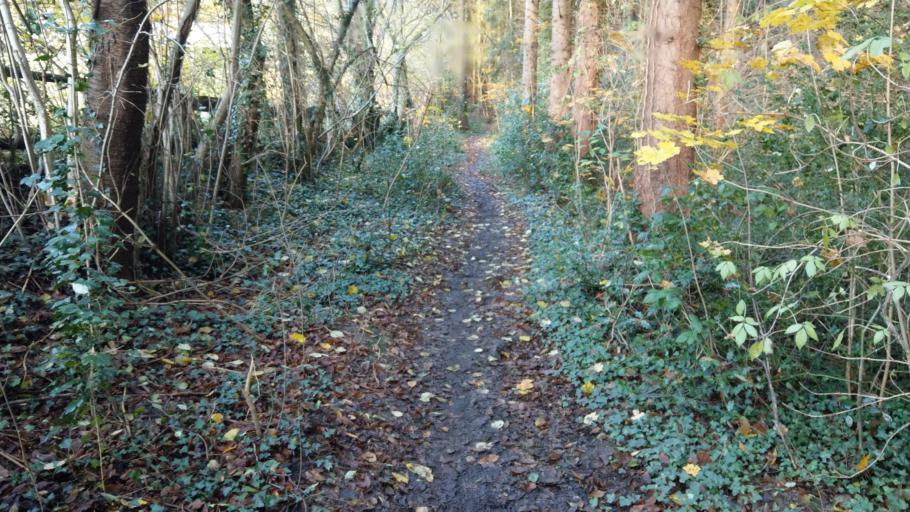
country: BE
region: Wallonia
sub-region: Province de Liege
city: La Calamine
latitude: 50.7271
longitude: 6.0094
